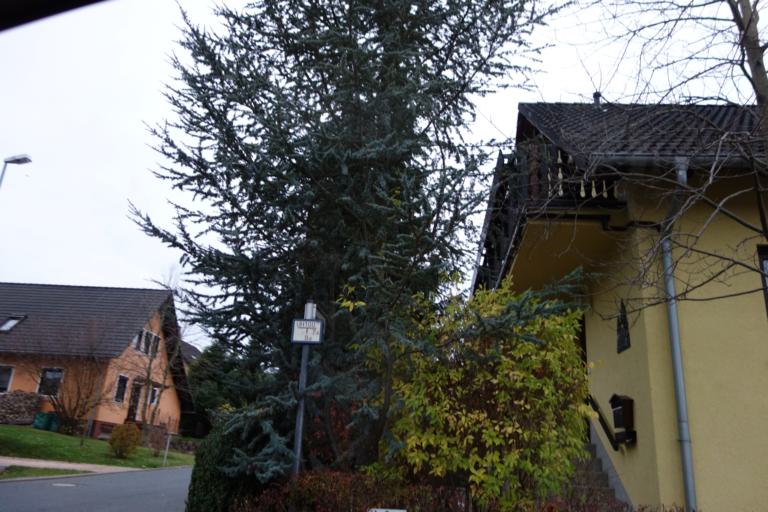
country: DE
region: Saxony
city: Falkenau
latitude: 50.8515
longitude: 13.1149
